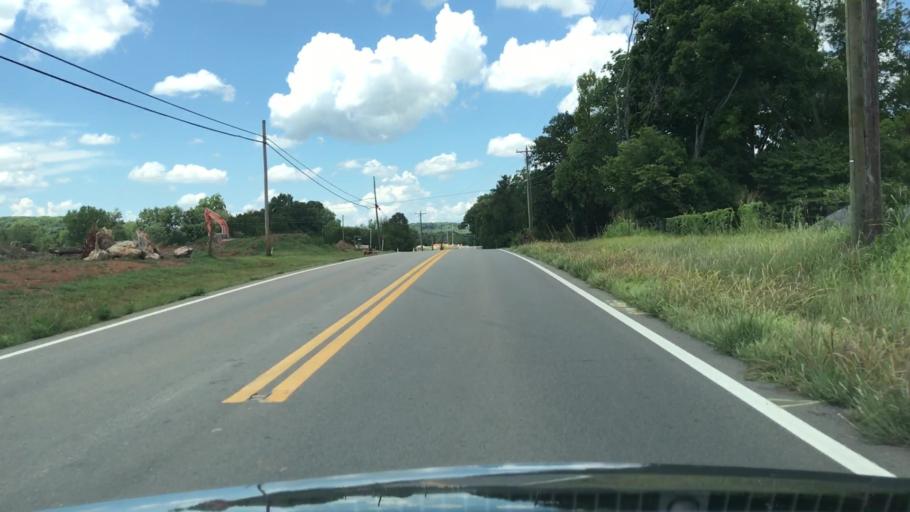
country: US
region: Tennessee
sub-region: Rutherford County
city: Smyrna
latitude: 35.8432
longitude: -86.5363
